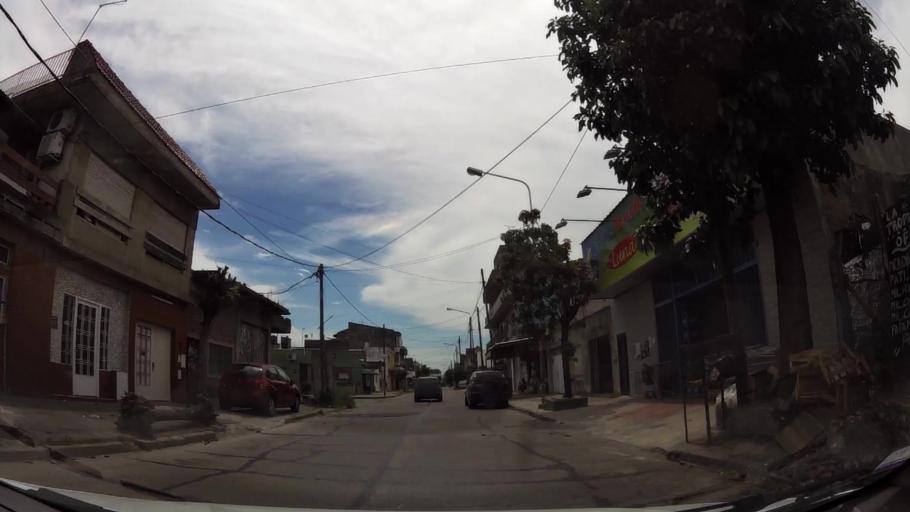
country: AR
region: Buenos Aires
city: San Justo
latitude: -34.6826
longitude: -58.5360
